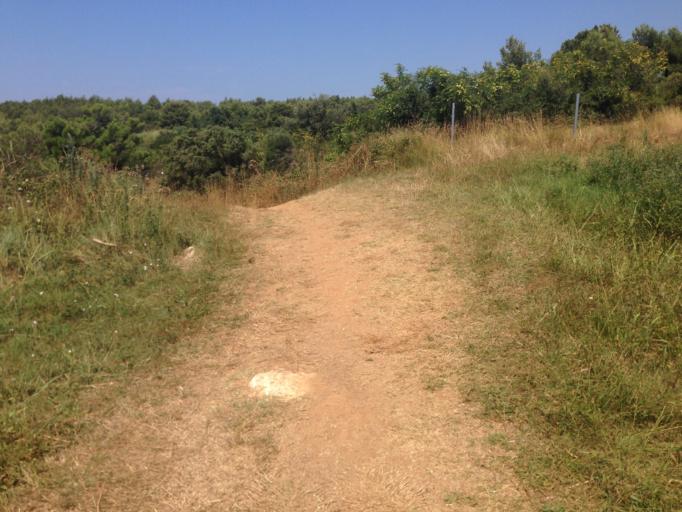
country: HR
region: Istarska
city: Medulin
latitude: 44.7866
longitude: 13.9082
